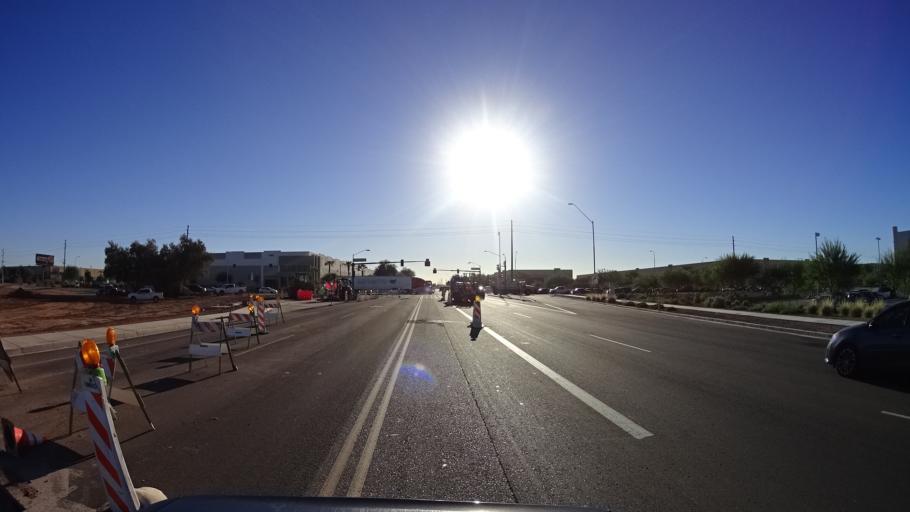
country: US
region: Arizona
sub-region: Maricopa County
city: Tolleson
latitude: 33.4371
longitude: -112.2220
